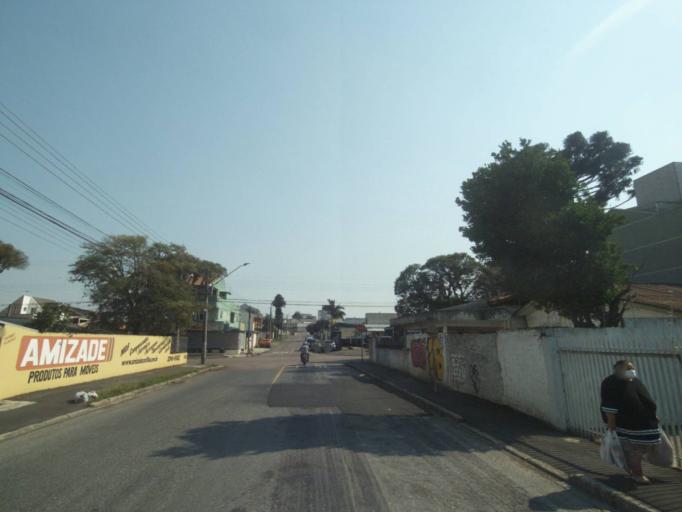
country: BR
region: Parana
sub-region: Sao Jose Dos Pinhais
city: Sao Jose dos Pinhais
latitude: -25.5102
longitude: -49.2831
